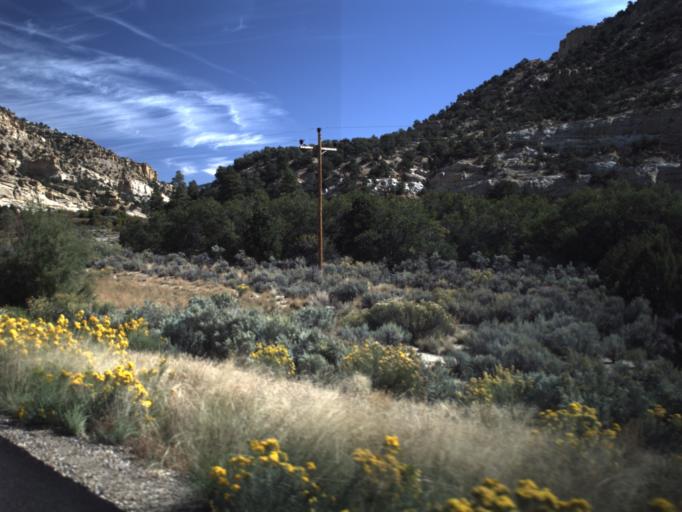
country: US
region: Utah
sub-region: Garfield County
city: Panguitch
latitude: 37.6000
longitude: -111.9180
